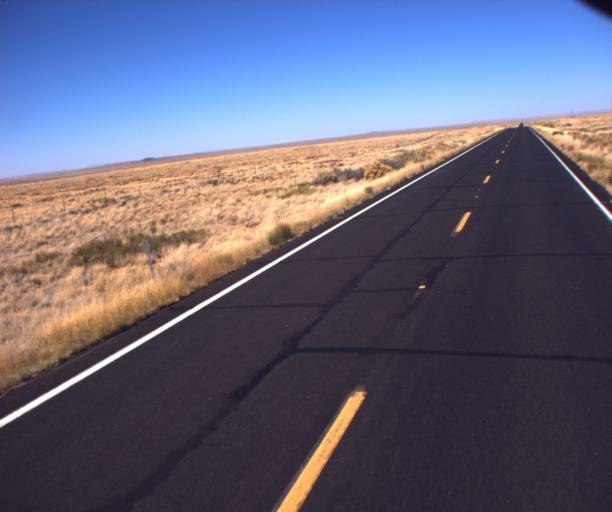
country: US
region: Arizona
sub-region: Navajo County
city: Dilkon
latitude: 35.5353
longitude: -110.4472
